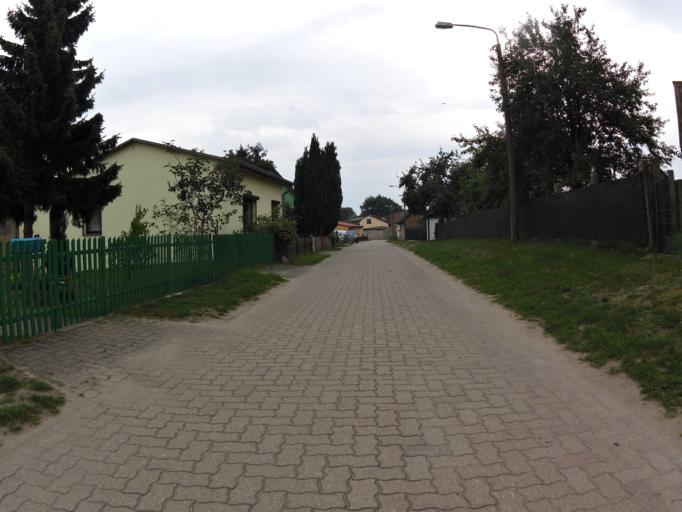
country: DE
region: Mecklenburg-Vorpommern
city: Seebad Heringsdorf
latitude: 53.8834
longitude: 14.1693
